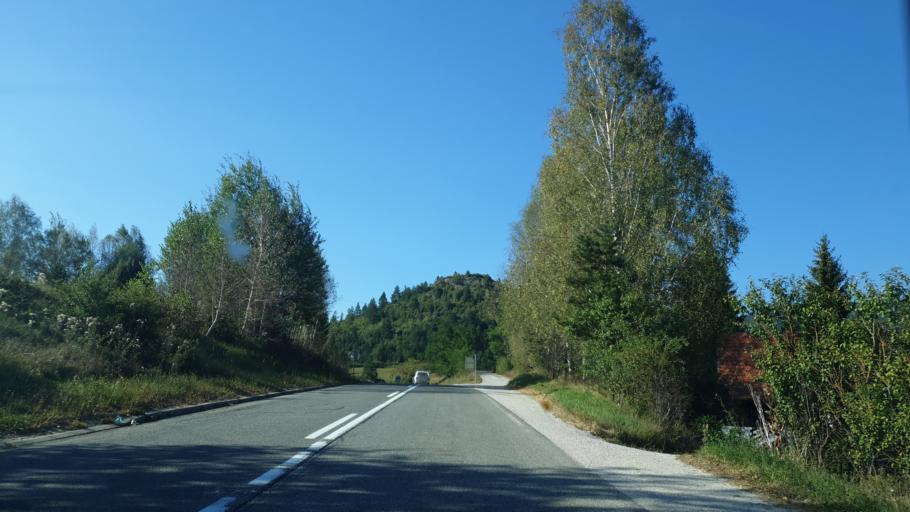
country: RS
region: Central Serbia
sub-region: Zlatiborski Okrug
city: Nova Varos
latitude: 43.5441
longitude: 19.7871
